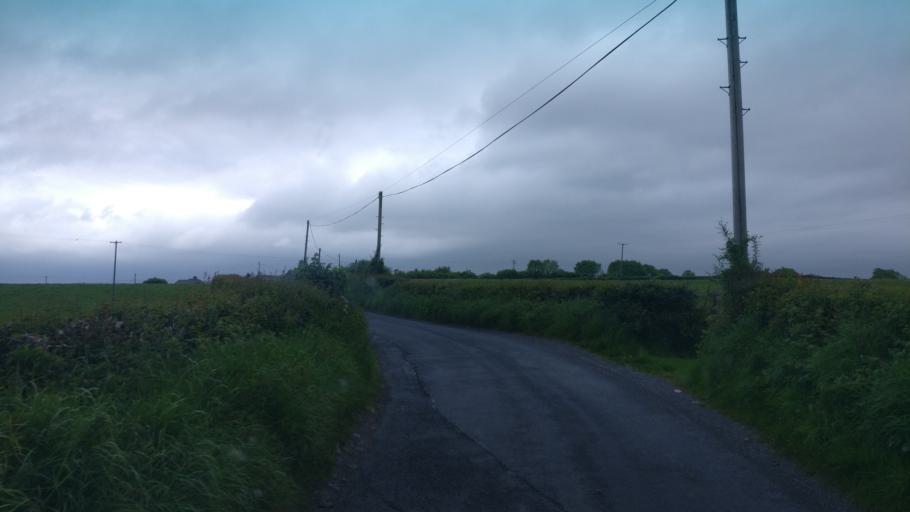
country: IE
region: Connaught
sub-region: County Galway
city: Portumna
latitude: 53.1429
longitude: -8.2878
